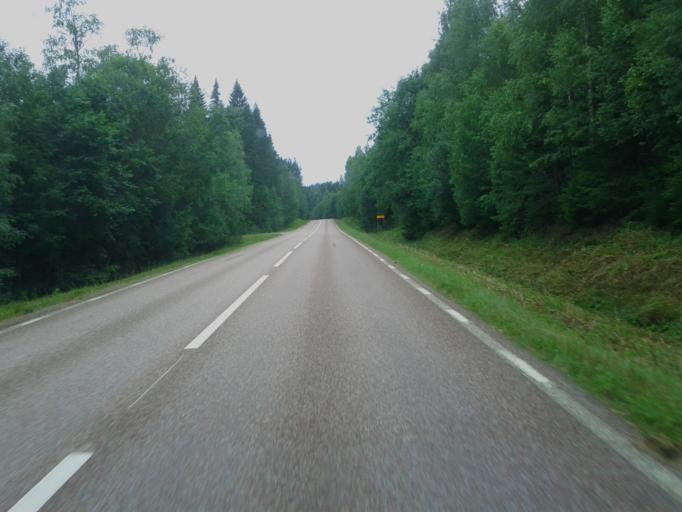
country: SE
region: Dalarna
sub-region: Borlange Kommun
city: Borlaenge
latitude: 60.3315
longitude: 15.3935
